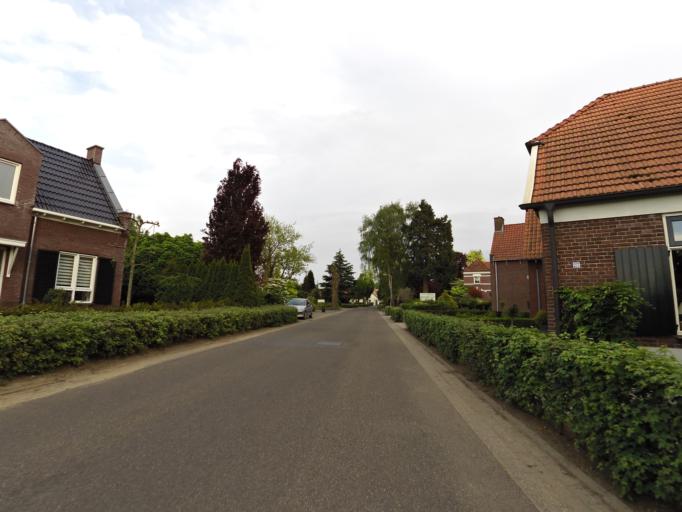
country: NL
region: Gelderland
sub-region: Oude IJsselstreek
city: Gendringen
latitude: 51.8411
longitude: 6.3906
